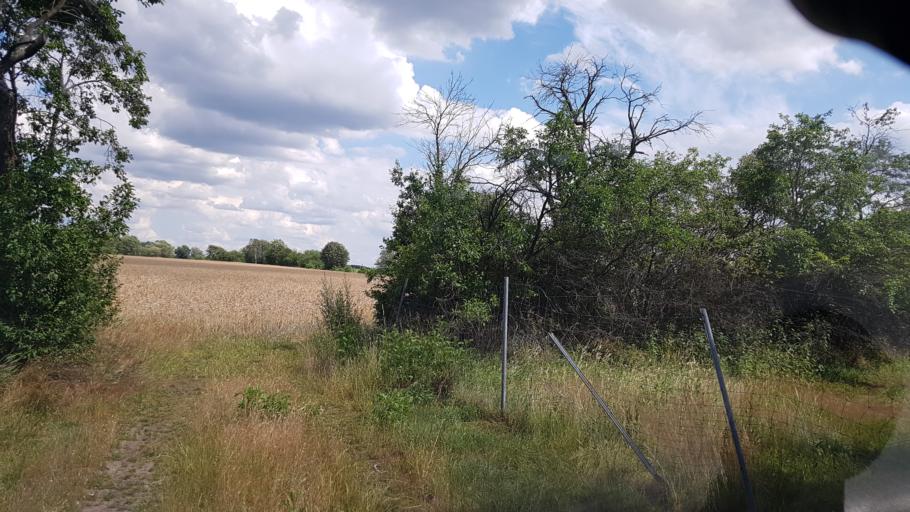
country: DE
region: Brandenburg
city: Finsterwalde
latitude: 51.6097
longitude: 13.7243
